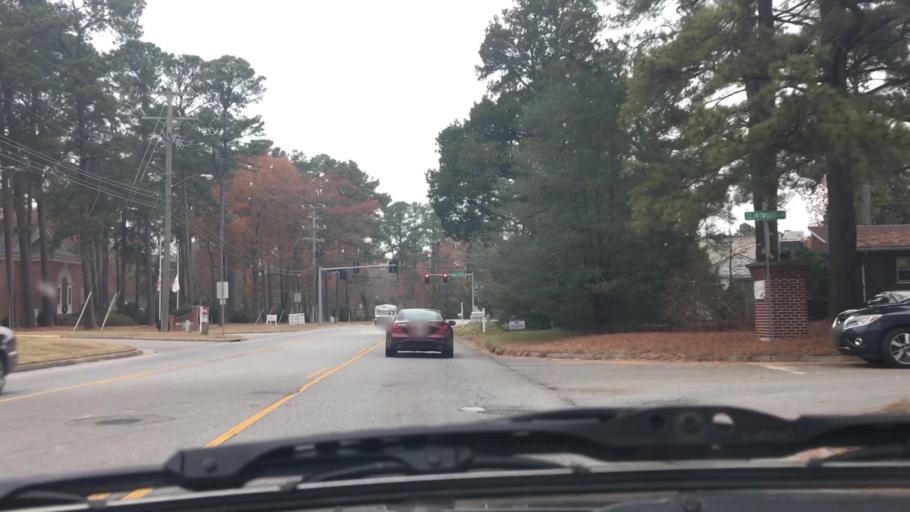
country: US
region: Virginia
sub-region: City of Portsmouth
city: Portsmouth Heights
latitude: 36.8549
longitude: -76.3788
